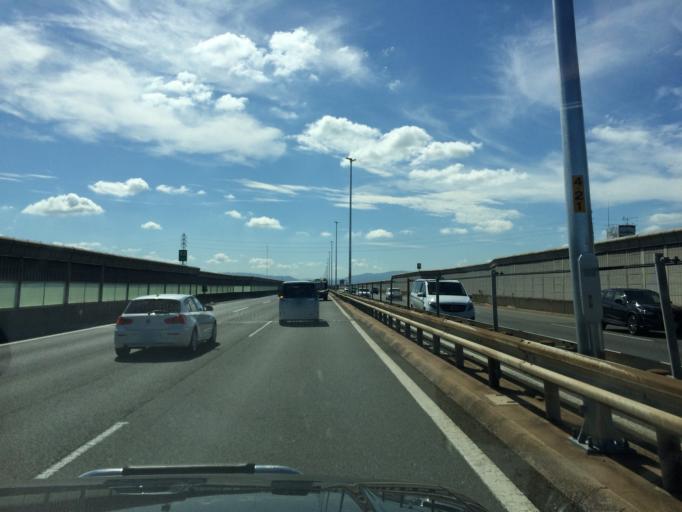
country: JP
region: Osaka
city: Matsubara
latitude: 34.5725
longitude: 135.5638
